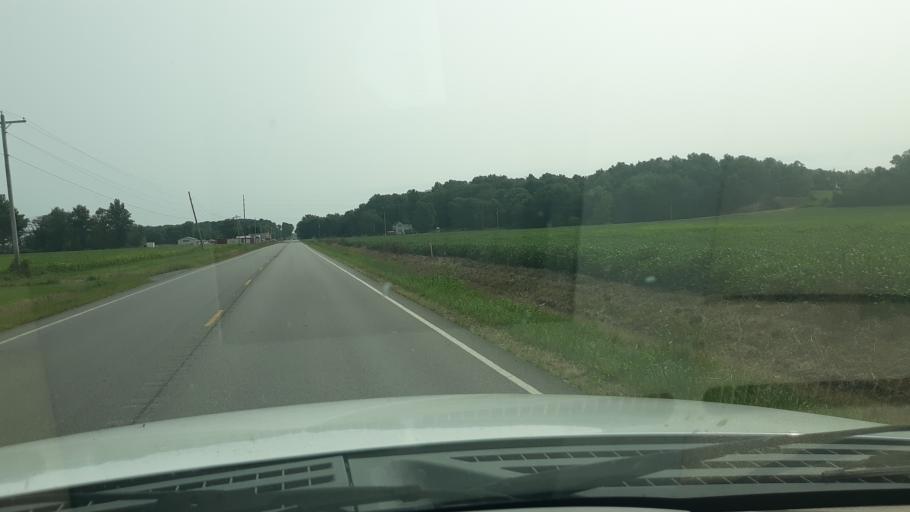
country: US
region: Indiana
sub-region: Gibson County
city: Owensville
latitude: 38.3559
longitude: -87.6774
